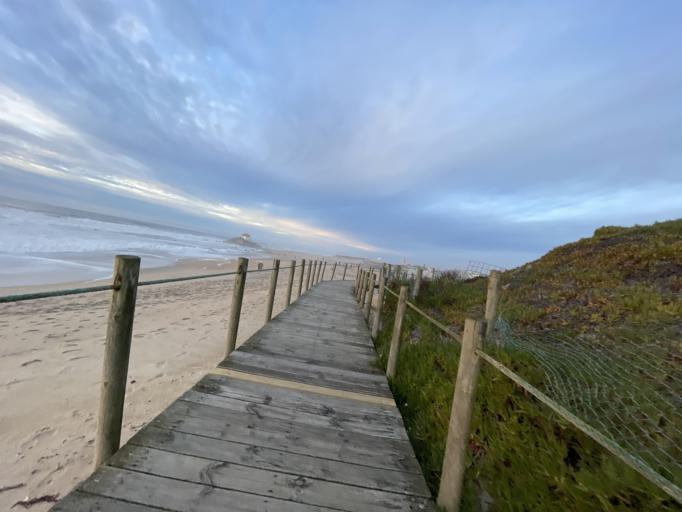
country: PT
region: Porto
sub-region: Vila Nova de Gaia
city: Vila Nova da Telha
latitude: 41.0660
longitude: -8.6566
